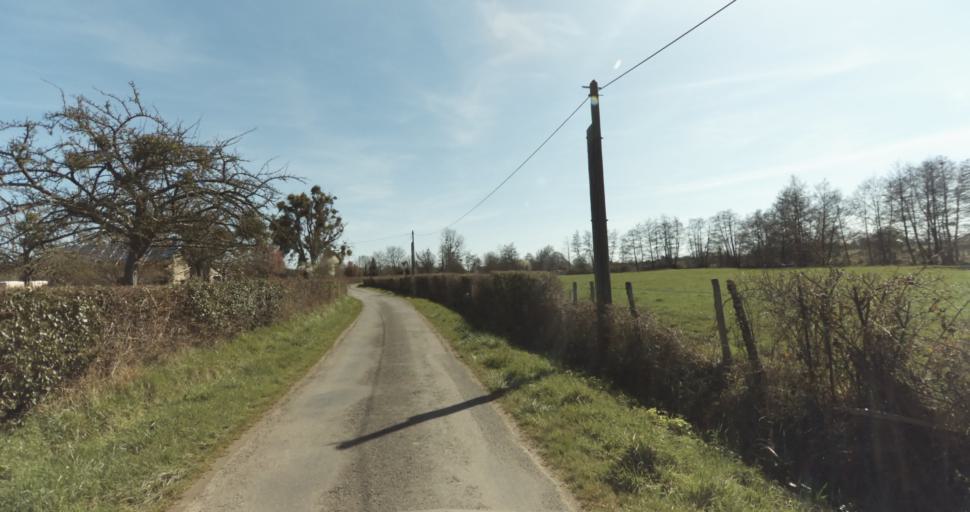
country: FR
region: Lower Normandy
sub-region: Departement du Calvados
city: Saint-Pierre-sur-Dives
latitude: 49.0616
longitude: -0.0274
